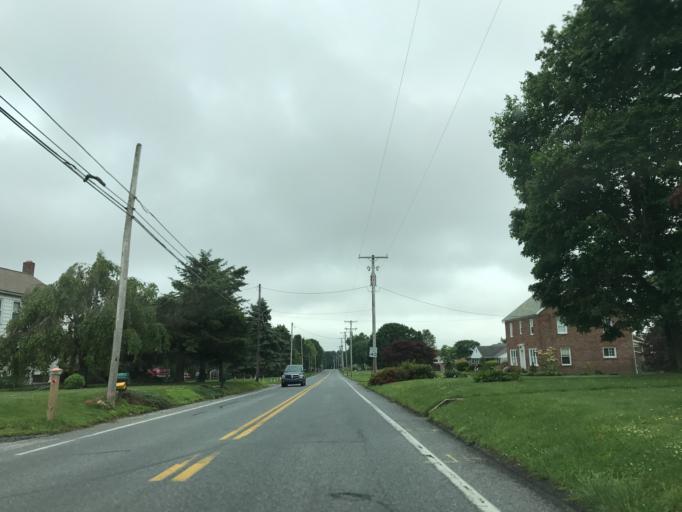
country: US
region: Pennsylvania
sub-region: York County
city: Stewartstown
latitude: 39.8055
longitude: -76.5968
